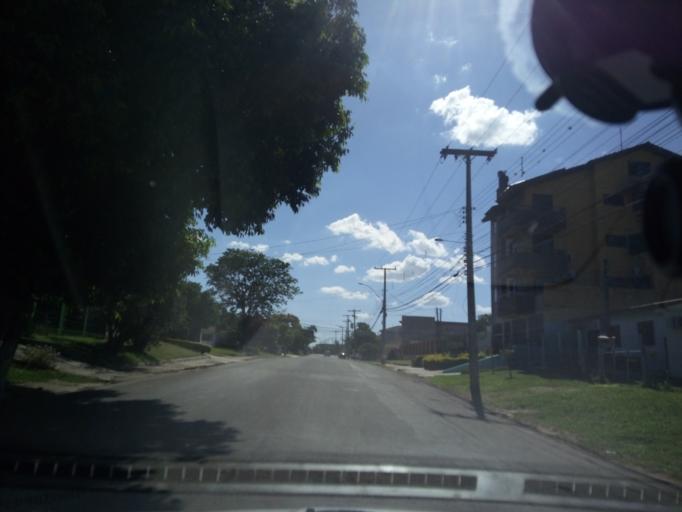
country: BR
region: Rio Grande do Sul
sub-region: Santa Maria
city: Santa Maria
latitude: -29.6986
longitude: -53.7148
